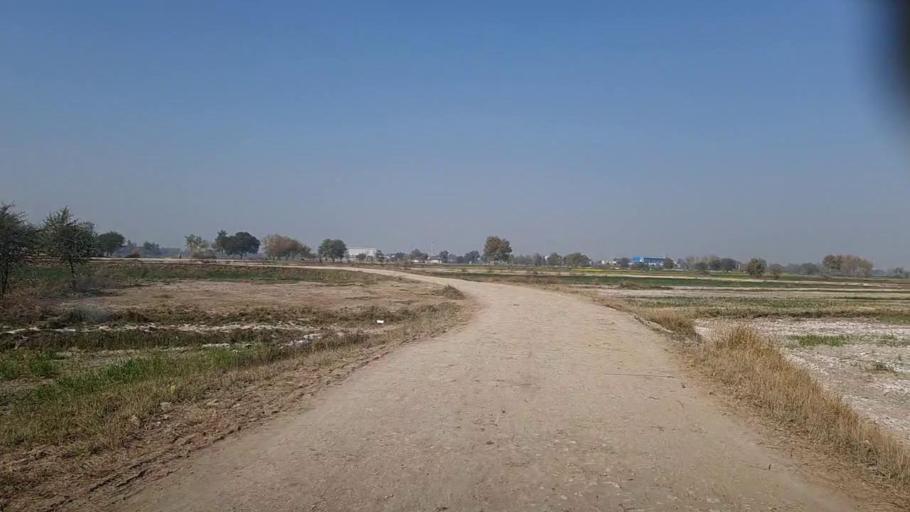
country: PK
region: Sindh
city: Khairpur
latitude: 27.9657
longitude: 69.7141
